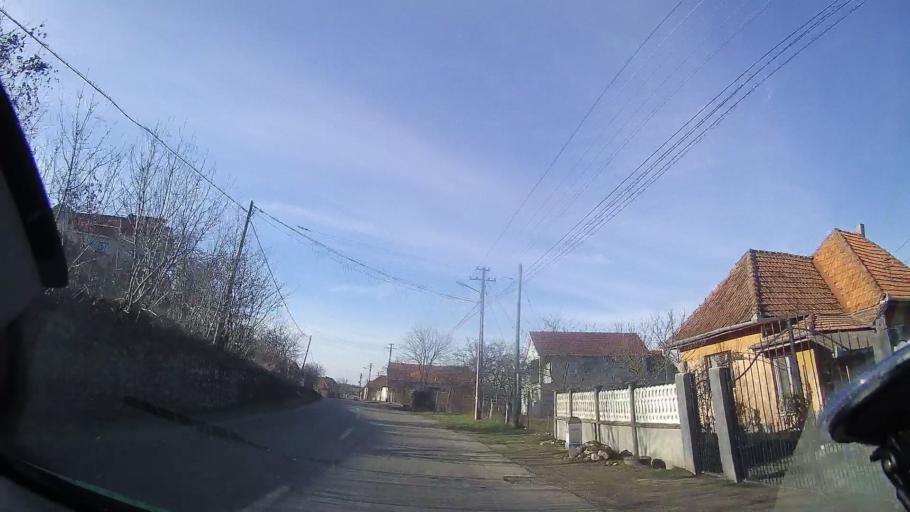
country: RO
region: Bihor
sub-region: Comuna Astileu
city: Astileu
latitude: 47.0280
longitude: 22.3959
